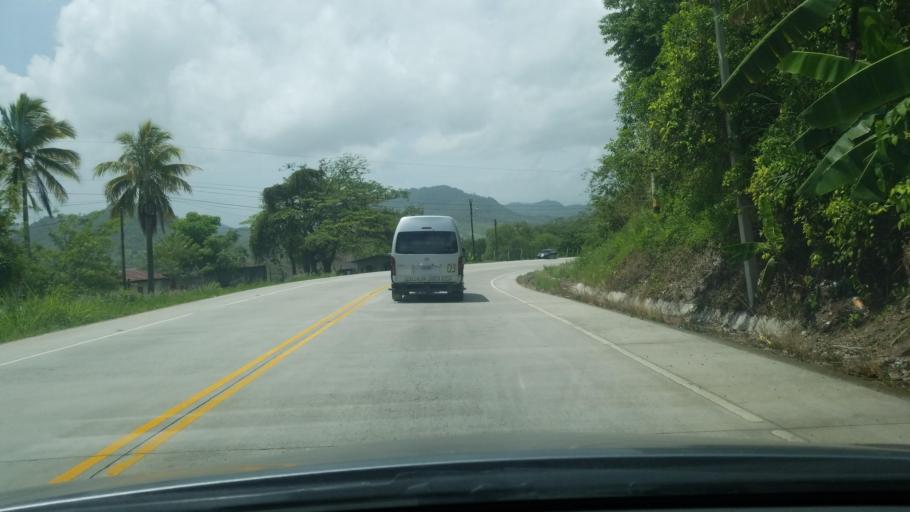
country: HN
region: Copan
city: San Juan de Planes
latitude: 14.9702
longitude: -88.7828
